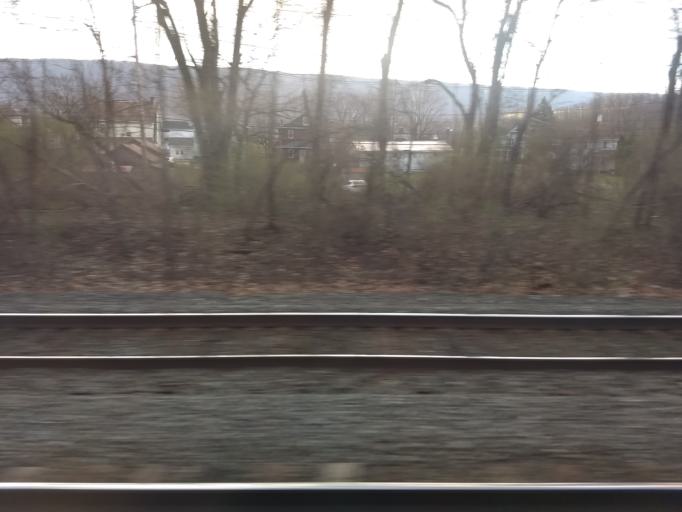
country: US
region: Pennsylvania
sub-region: Blair County
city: Bellwood
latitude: 40.5973
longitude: -78.3366
